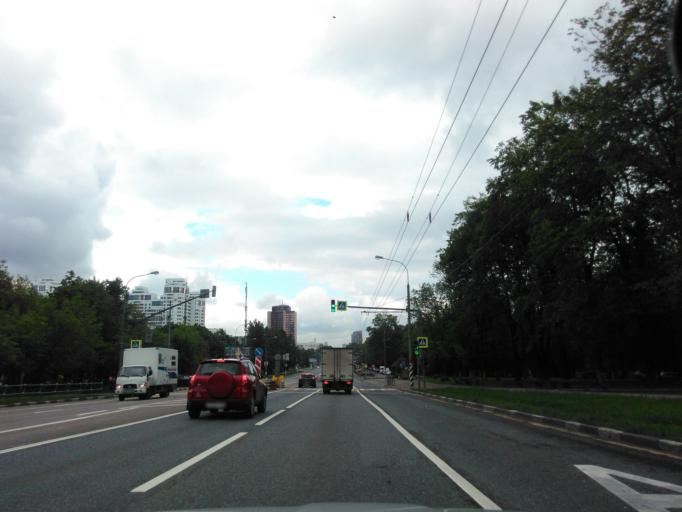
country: RU
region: Moscow
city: Zyuzino
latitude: 55.6588
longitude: 37.5736
